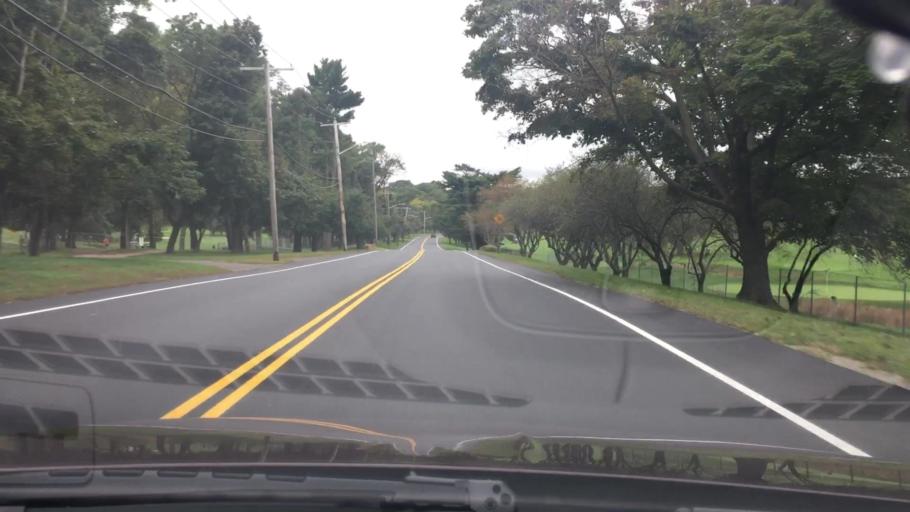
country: US
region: New York
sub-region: Nassau County
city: Farmingdale
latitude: 40.7456
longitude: -73.4507
